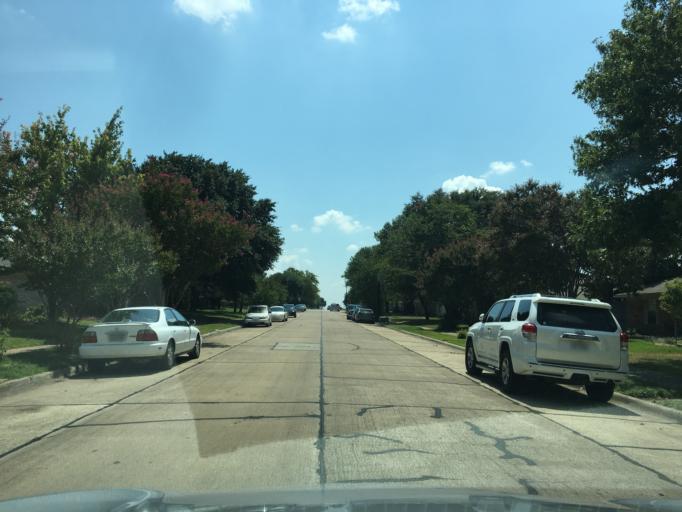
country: US
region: Texas
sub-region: Dallas County
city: Garland
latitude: 32.9396
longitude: -96.6571
